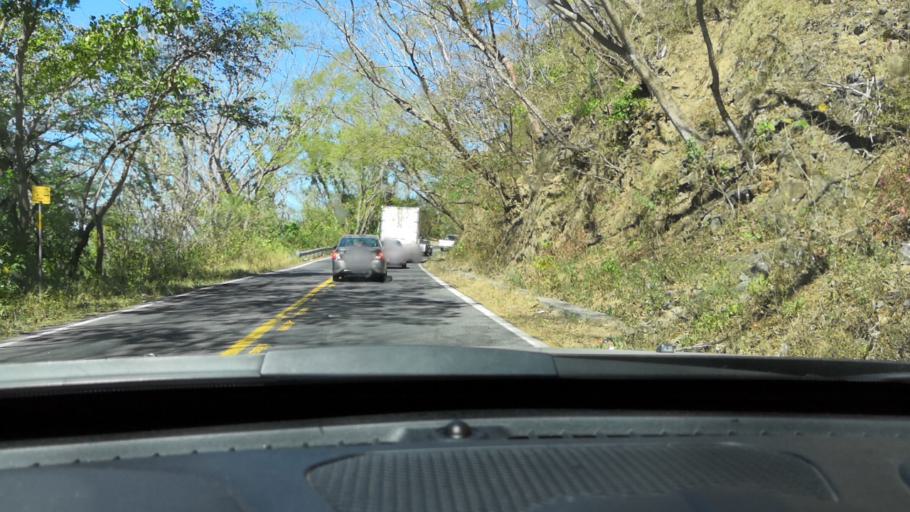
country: MX
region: Nayarit
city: Compostela
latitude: 21.2164
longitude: -104.9952
